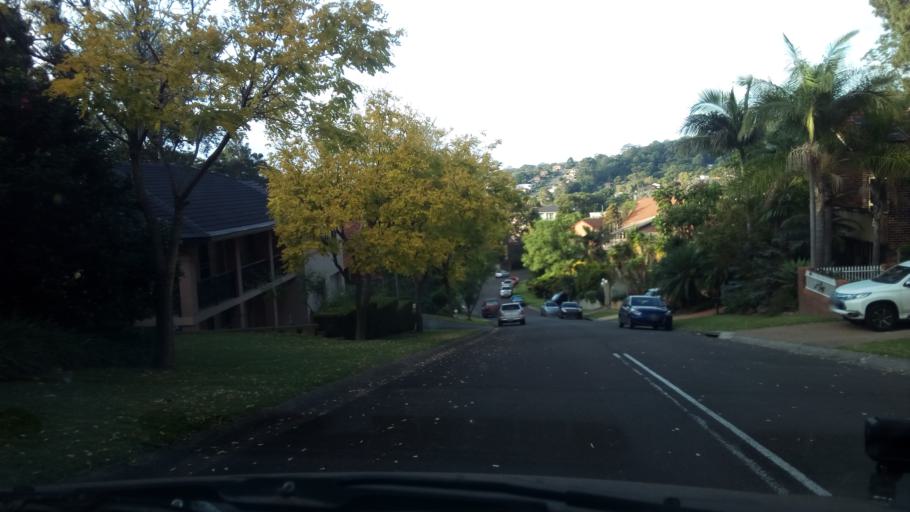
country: AU
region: New South Wales
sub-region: Wollongong
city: Mount Ousley
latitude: -34.3809
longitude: 150.8685
